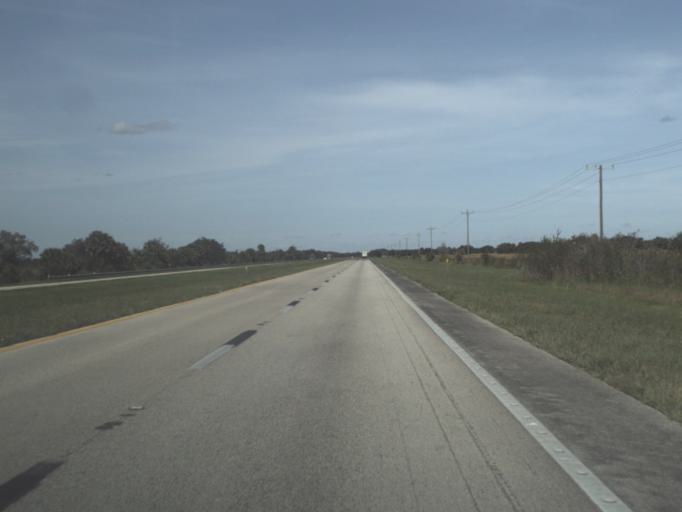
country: US
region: Florida
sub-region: Glades County
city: Moore Haven
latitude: 26.8741
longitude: -81.2221
